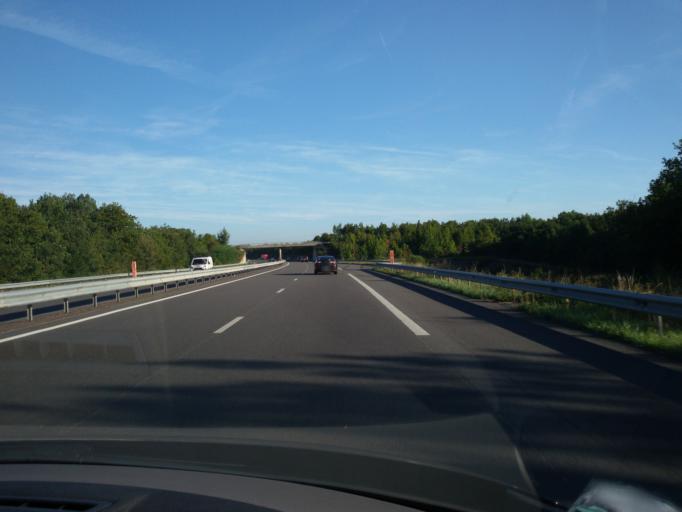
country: FR
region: Centre
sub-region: Departement du Cher
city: Plaimpied-Givaudins
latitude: 46.9737
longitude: 2.4244
